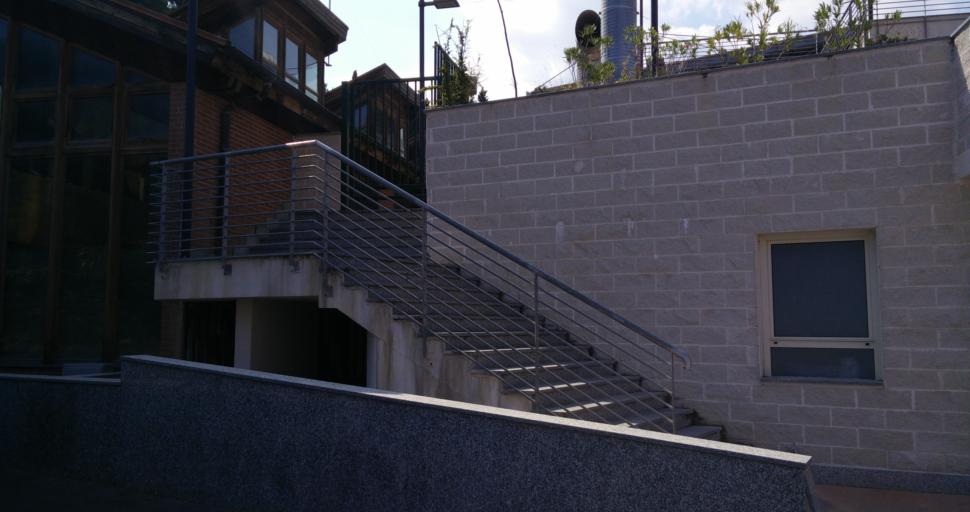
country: IT
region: Liguria
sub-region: Provincia di Savona
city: Alassio
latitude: 44.0005
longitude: 8.1639
